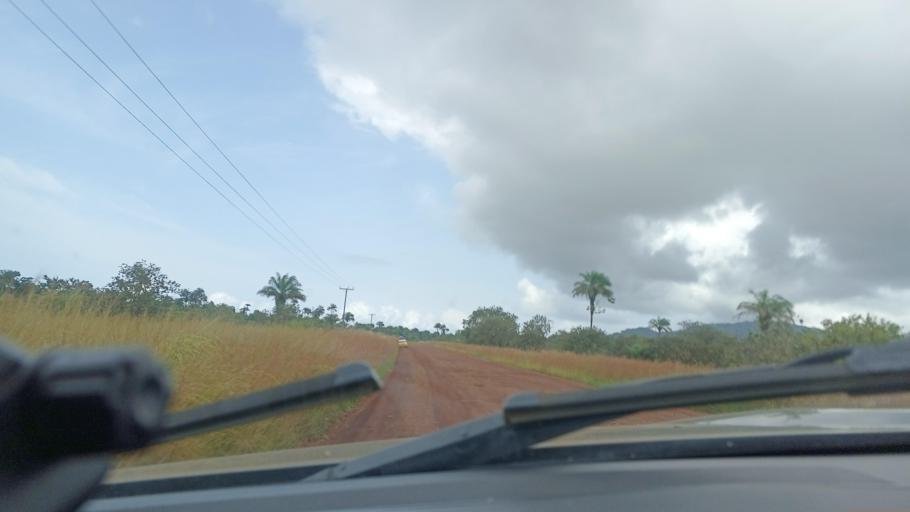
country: LR
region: Grand Cape Mount
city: Robertsport
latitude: 6.7032
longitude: -11.3154
